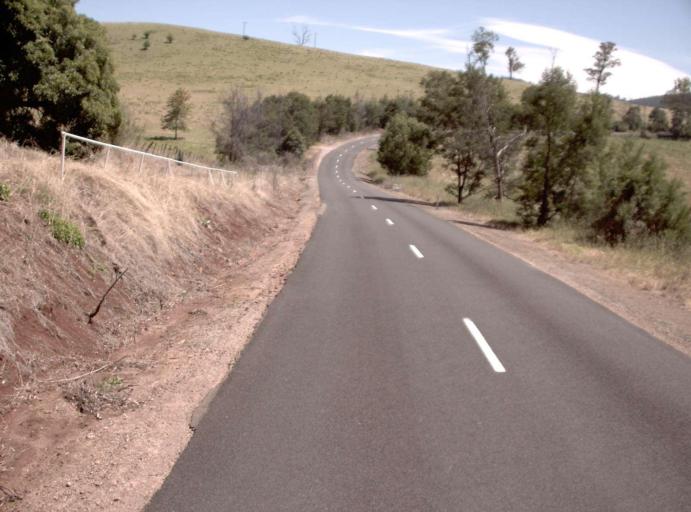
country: AU
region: Victoria
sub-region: East Gippsland
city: Lakes Entrance
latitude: -37.4060
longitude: 148.2115
